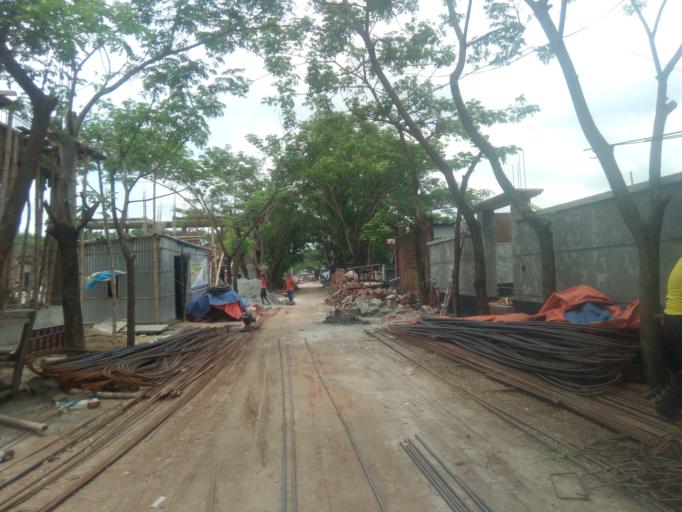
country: BD
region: Dhaka
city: Azimpur
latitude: 23.7540
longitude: 90.3488
